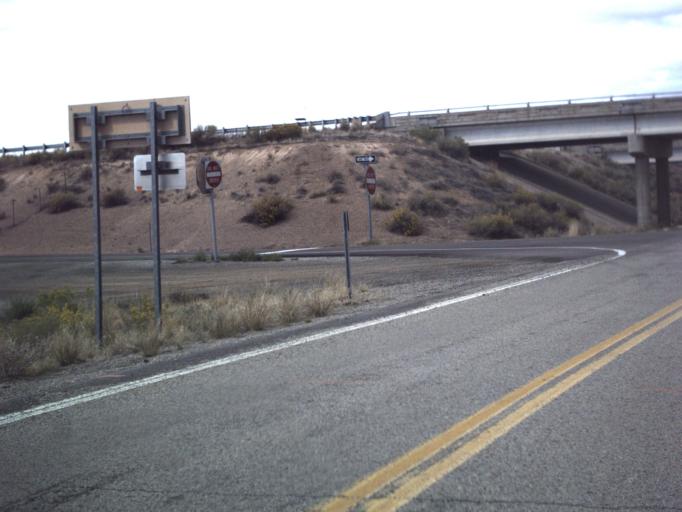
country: US
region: Colorado
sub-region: Mesa County
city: Loma
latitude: 39.0367
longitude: -109.2822
